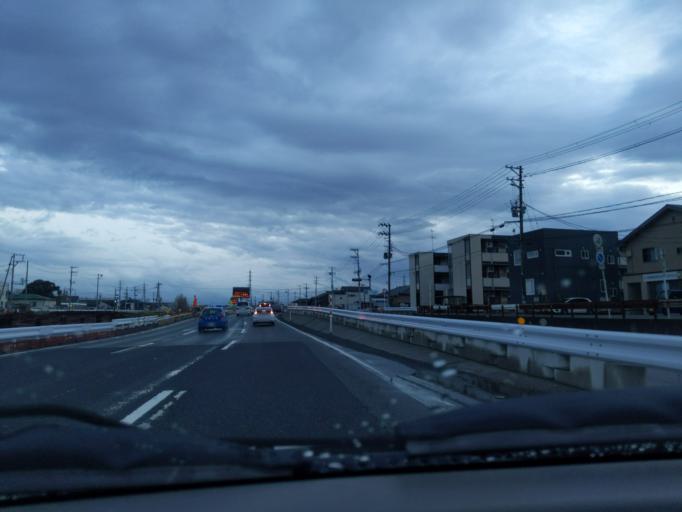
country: JP
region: Niigata
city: Niigata-shi
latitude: 37.9089
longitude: 139.0727
